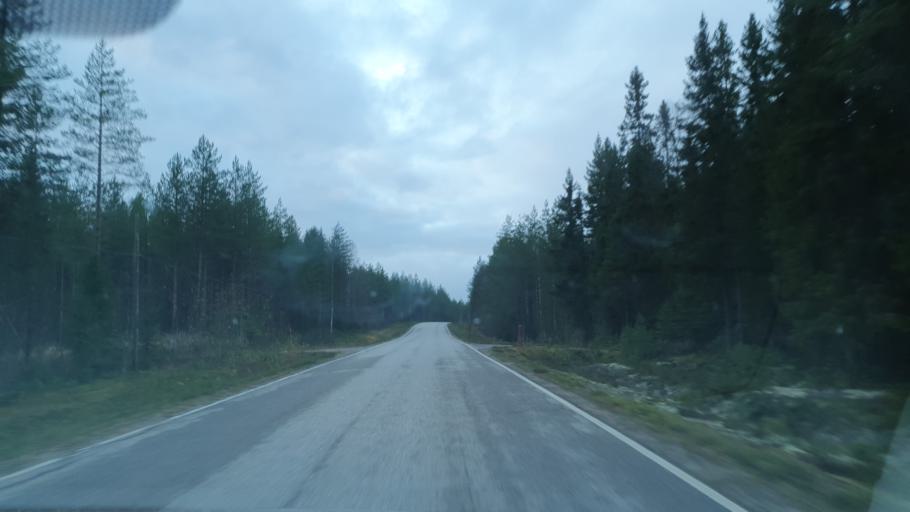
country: FI
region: Kainuu
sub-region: Kajaani
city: Ristijaervi
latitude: 64.4295
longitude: 28.3742
